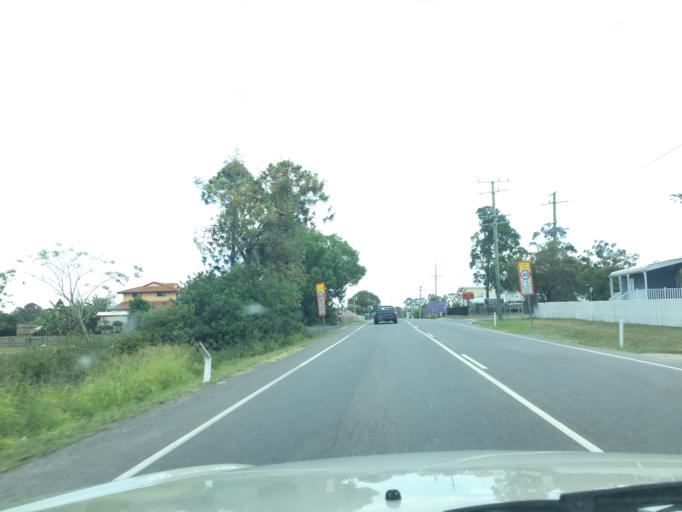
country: AU
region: Queensland
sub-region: Logan
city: Waterford West
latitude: -27.6973
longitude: 153.1451
